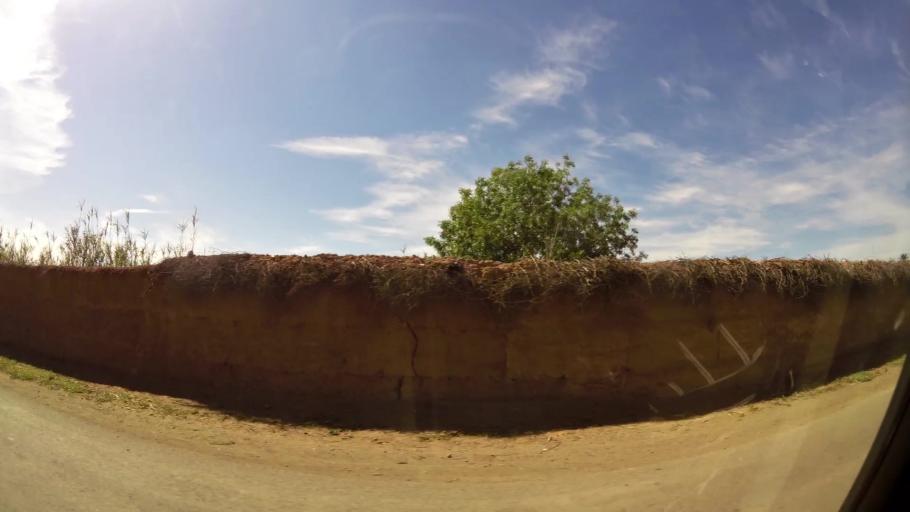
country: MA
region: Marrakech-Tensift-Al Haouz
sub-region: Marrakech
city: Marrakesh
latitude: 31.6326
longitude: -7.9550
